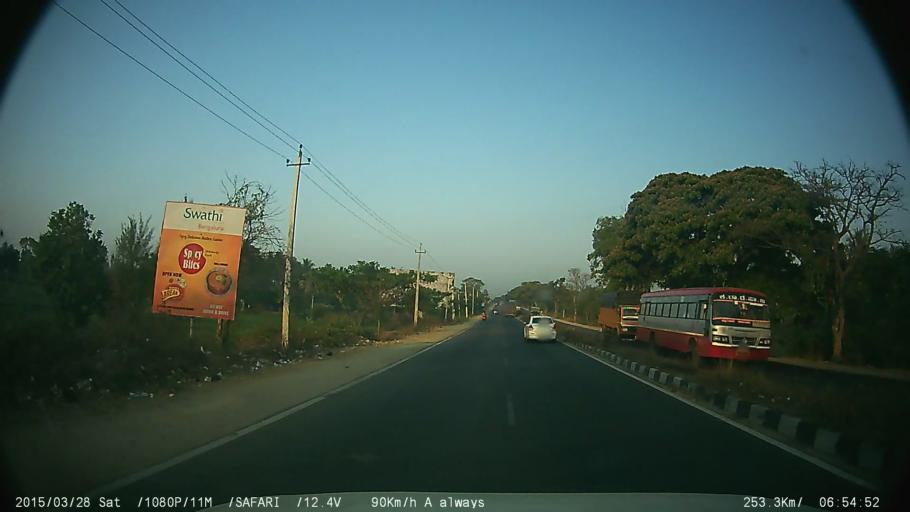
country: IN
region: Karnataka
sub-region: Mandya
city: Maddur
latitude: 12.5772
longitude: 77.0226
